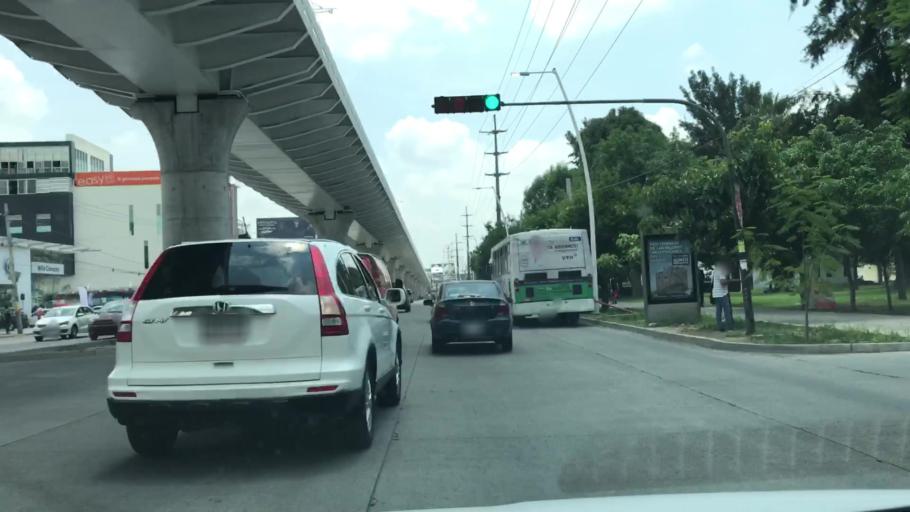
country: MX
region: Jalisco
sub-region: Zapopan
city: Zapopan
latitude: 20.7025
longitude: -103.3600
